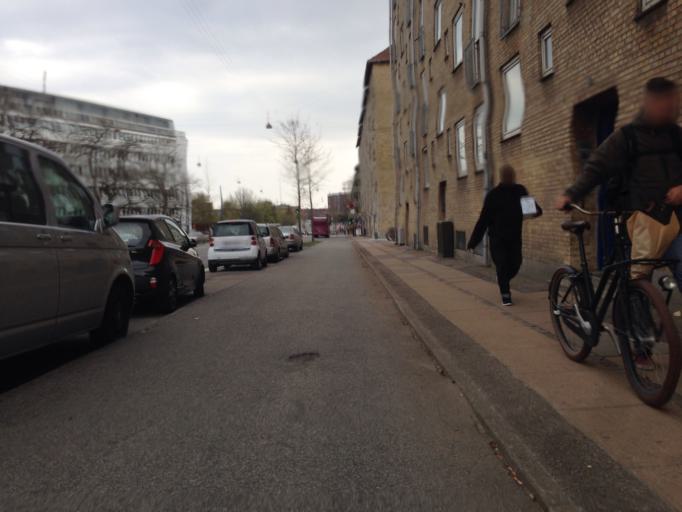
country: DK
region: Capital Region
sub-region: Frederiksberg Kommune
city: Frederiksberg
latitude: 55.7115
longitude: 12.5367
